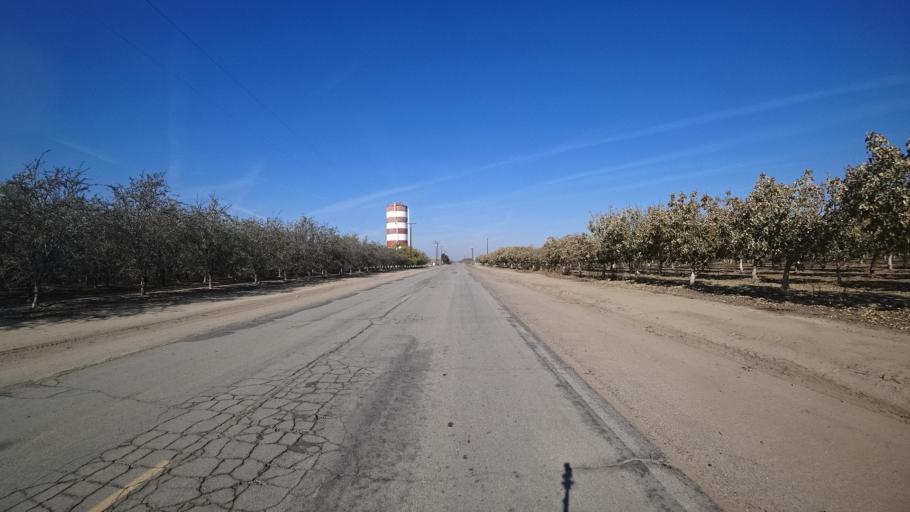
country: US
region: California
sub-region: Kern County
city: Wasco
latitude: 35.6578
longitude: -119.3486
